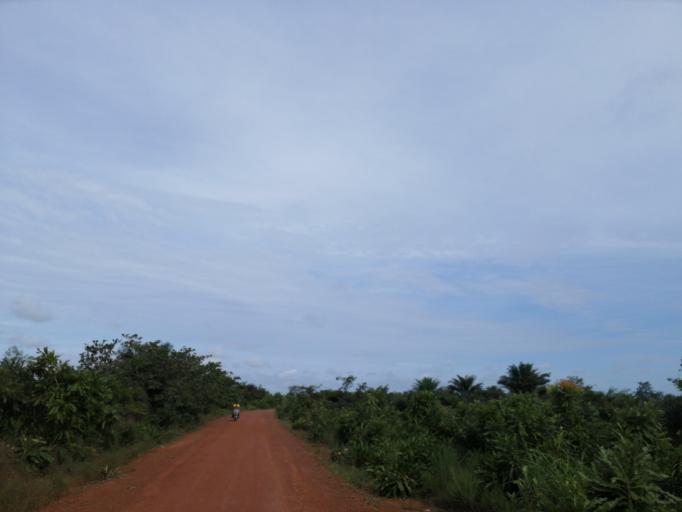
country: SL
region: Northern Province
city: Port Loko
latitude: 8.7692
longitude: -12.9111
